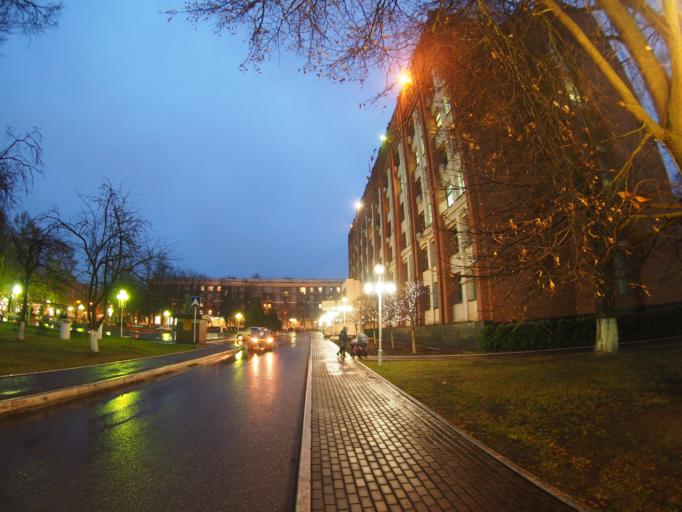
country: RU
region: Moskovskaya
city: Stupino
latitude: 54.8868
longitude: 38.0766
